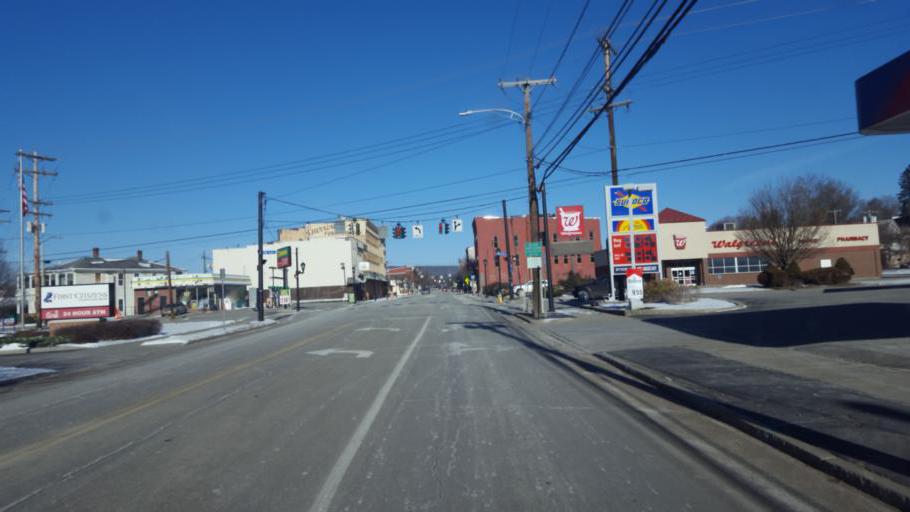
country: US
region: New York
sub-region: Allegany County
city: Wellsville
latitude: 42.1194
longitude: -77.9439
